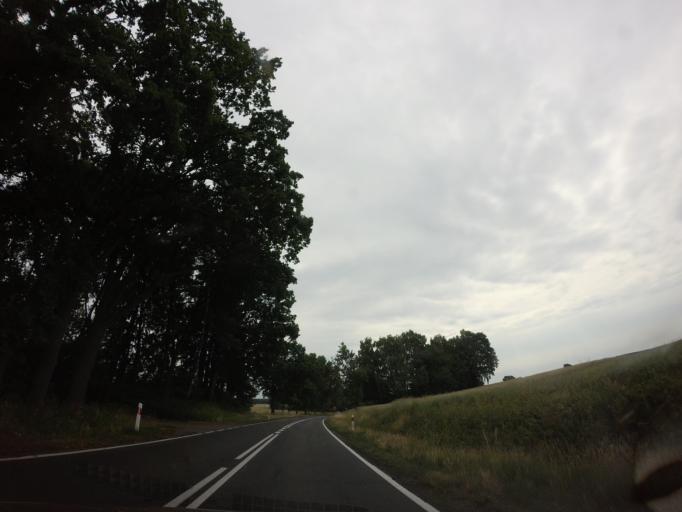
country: PL
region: West Pomeranian Voivodeship
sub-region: Powiat szczecinecki
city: Lubowo
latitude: 53.5915
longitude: 16.3538
